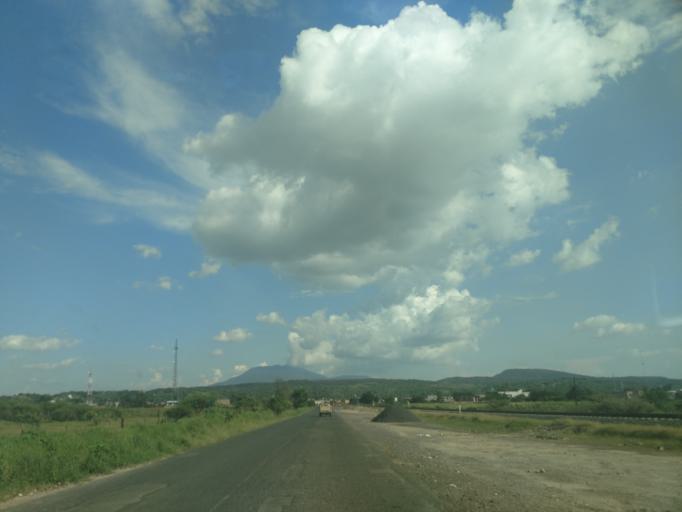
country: MX
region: Jalisco
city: Antonio Escobedo
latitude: 20.9083
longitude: -103.9879
